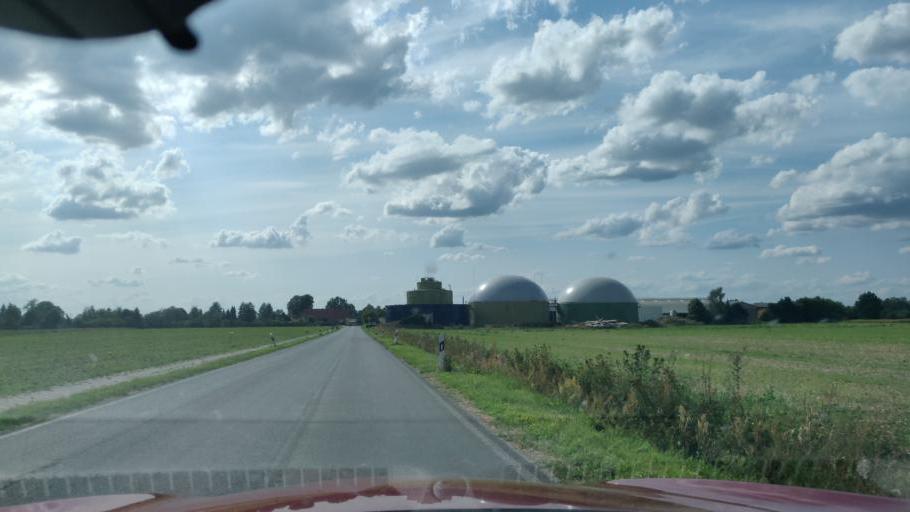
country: DE
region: Saxony
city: Schildau
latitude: 51.4821
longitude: 12.9125
